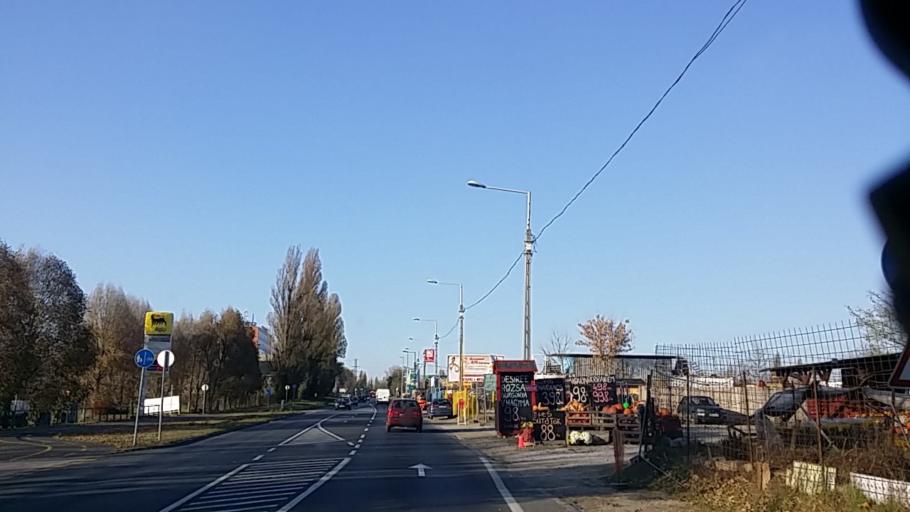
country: HU
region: Budapest
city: Budapest XVII. keruelet
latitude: 47.4924
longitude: 19.2423
